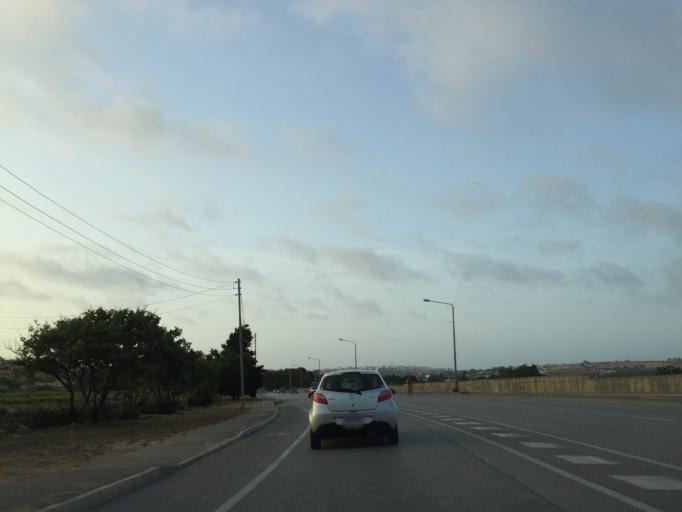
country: MT
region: Il-Mosta
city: Mosta
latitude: 35.9204
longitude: 14.4156
